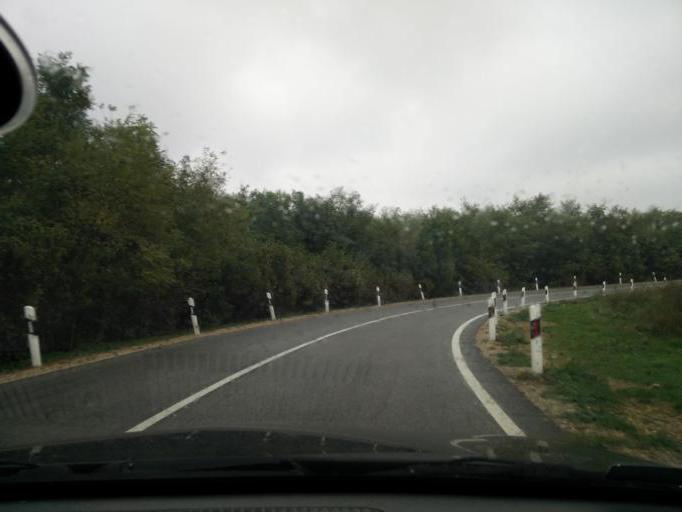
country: HU
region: Komarom-Esztergom
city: Bajna
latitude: 47.6361
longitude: 18.5558
